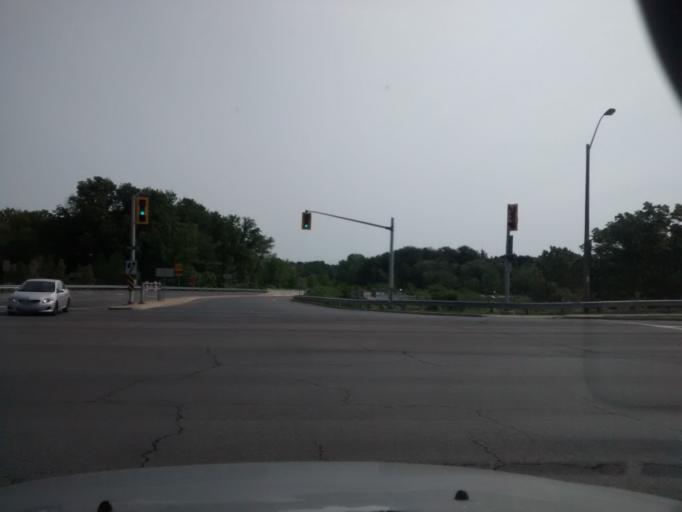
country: CA
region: Ontario
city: Hamilton
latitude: 43.2268
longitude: -79.7914
